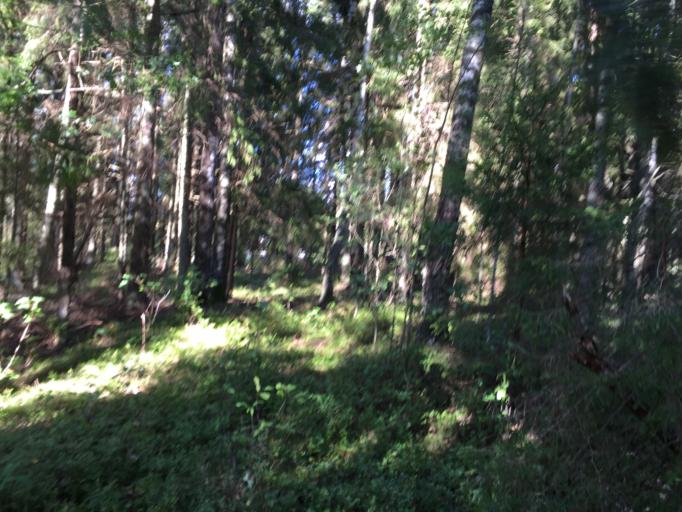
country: LV
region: Kuldigas Rajons
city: Kuldiga
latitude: 57.0045
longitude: 21.7889
